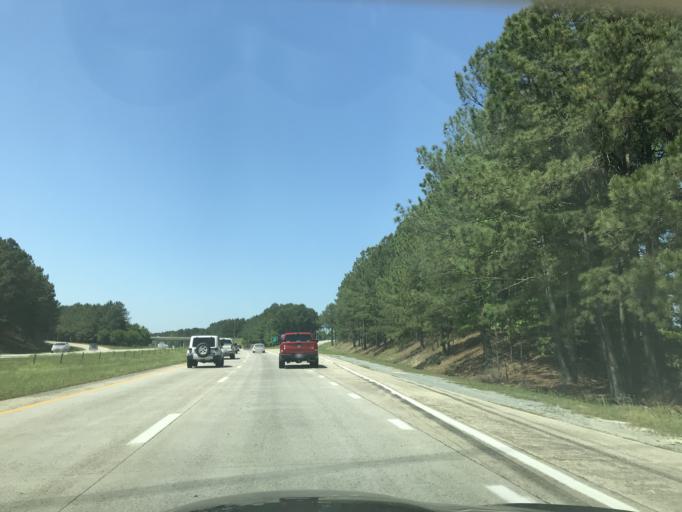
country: US
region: North Carolina
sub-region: Johnston County
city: Benson
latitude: 35.5126
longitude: -78.5560
